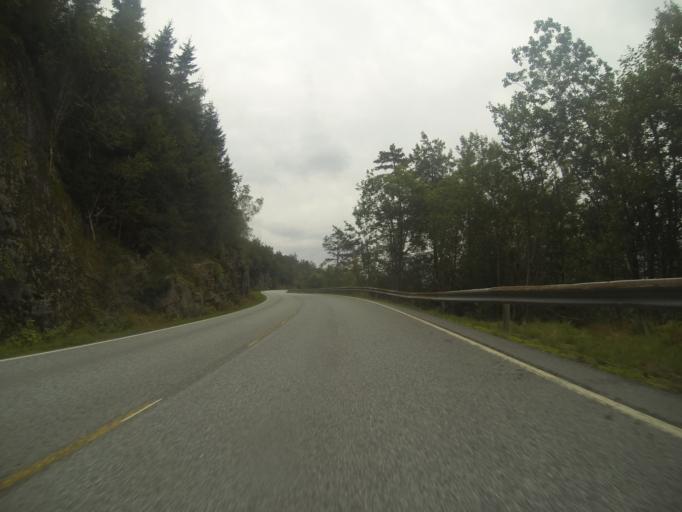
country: NO
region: Rogaland
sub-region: Suldal
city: Sand
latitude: 59.5526
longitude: 6.2605
